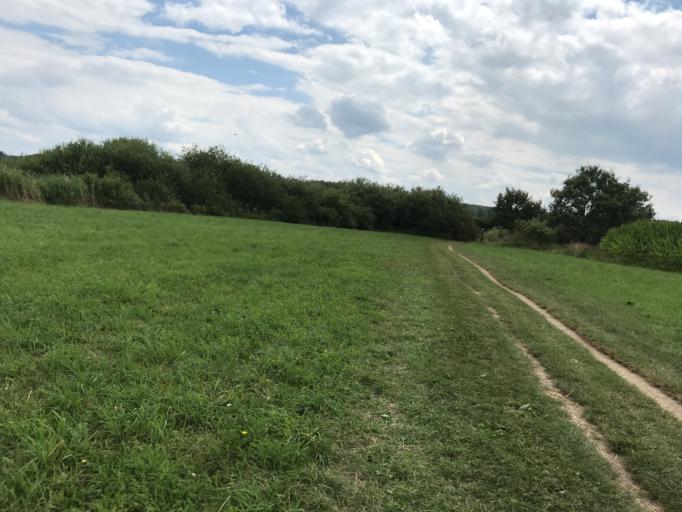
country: CZ
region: Jihocesky
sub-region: Okres Jindrichuv Hradec
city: Trebon
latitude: 48.9939
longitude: 14.7381
